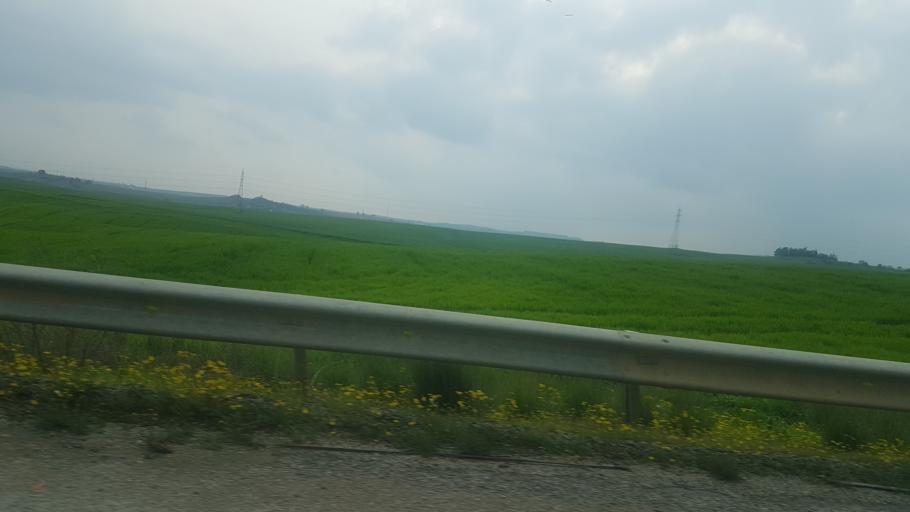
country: TR
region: Mersin
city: Yenice
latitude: 37.0718
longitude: 35.1706
